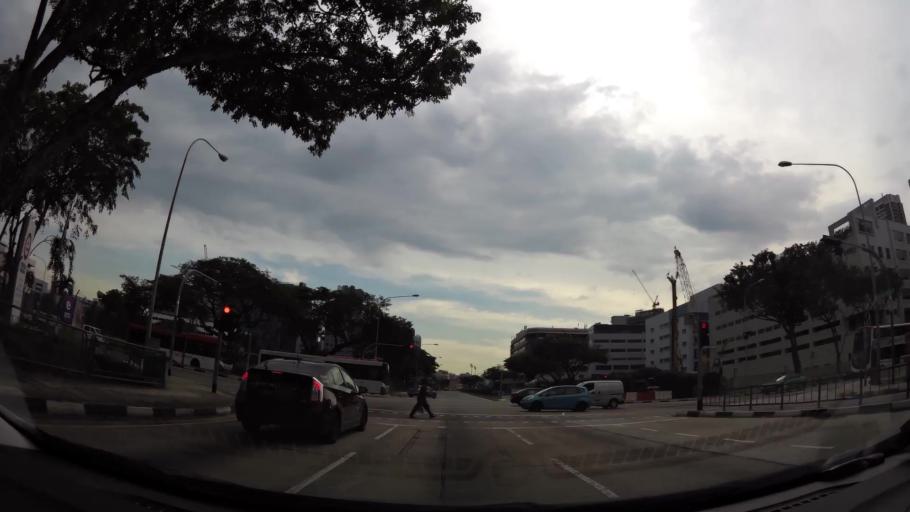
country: SG
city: Singapore
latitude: 1.3155
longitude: 103.8646
